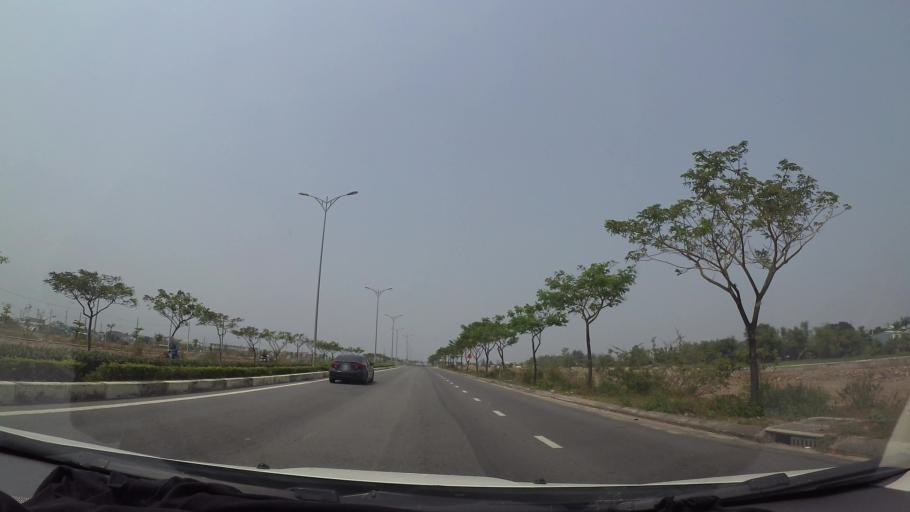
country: VN
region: Da Nang
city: Ngu Hanh Son
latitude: 15.9898
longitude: 108.2385
